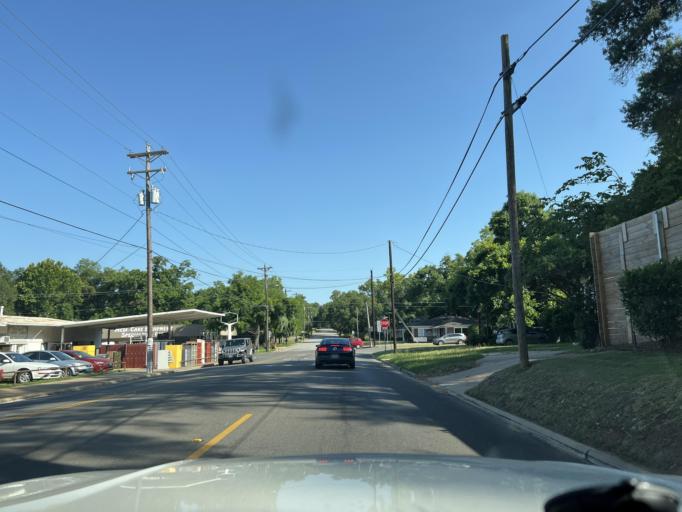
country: US
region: Texas
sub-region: Washington County
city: Brenham
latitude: 30.1572
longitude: -96.3975
